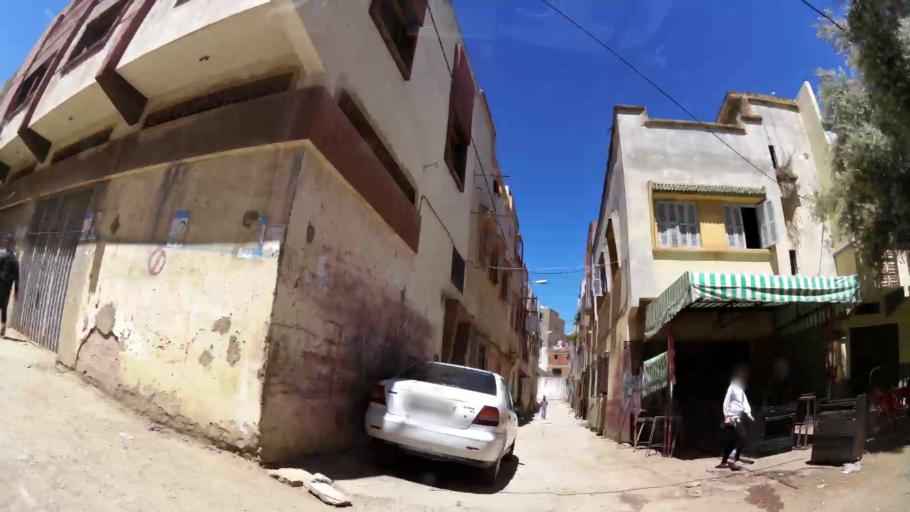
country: MA
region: Meknes-Tafilalet
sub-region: Meknes
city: Meknes
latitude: 33.9058
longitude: -5.5774
